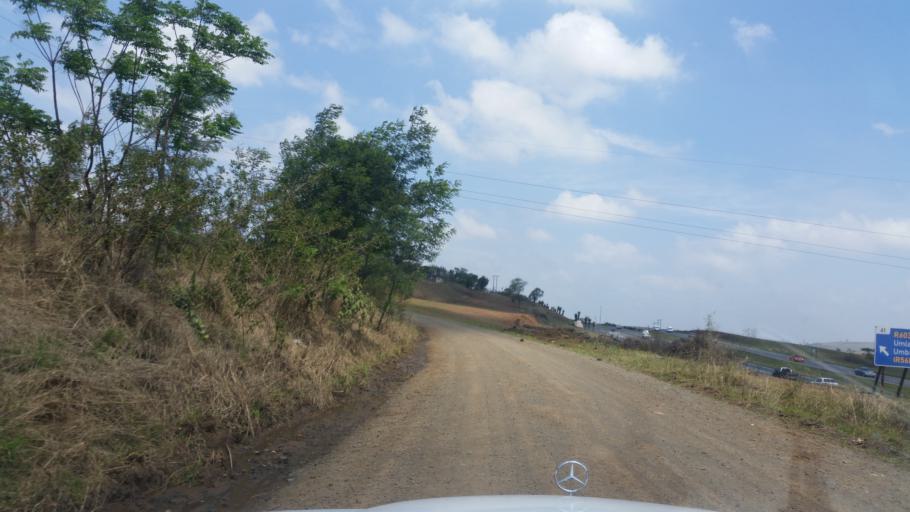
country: ZA
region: KwaZulu-Natal
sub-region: uMgungundlovu District Municipality
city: Camperdown
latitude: -29.7102
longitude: 30.4968
